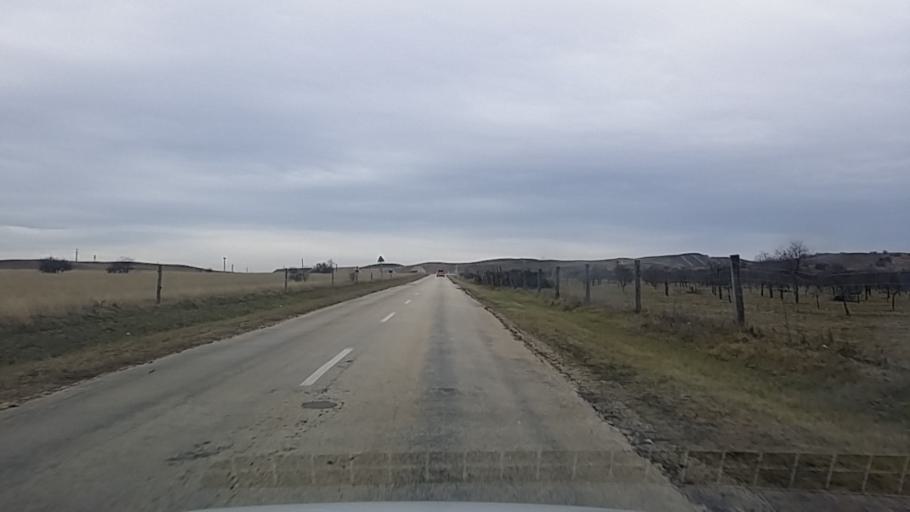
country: HU
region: Fejer
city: Zamoly
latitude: 47.3405
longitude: 18.3623
